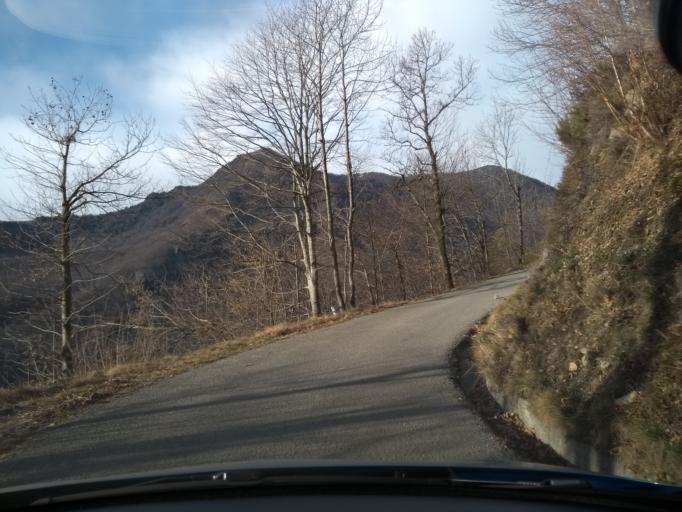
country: IT
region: Piedmont
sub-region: Provincia di Torino
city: Cantoira
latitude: 45.3465
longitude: 7.3819
